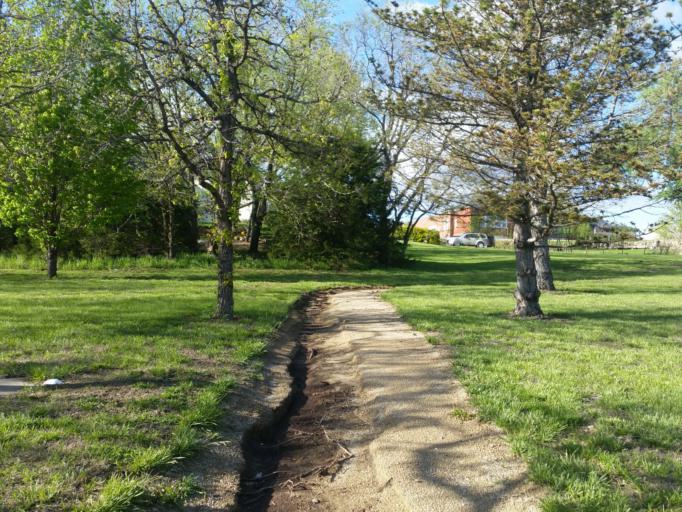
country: US
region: Kansas
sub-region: Riley County
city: Ogden
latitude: 39.2245
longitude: -96.7110
